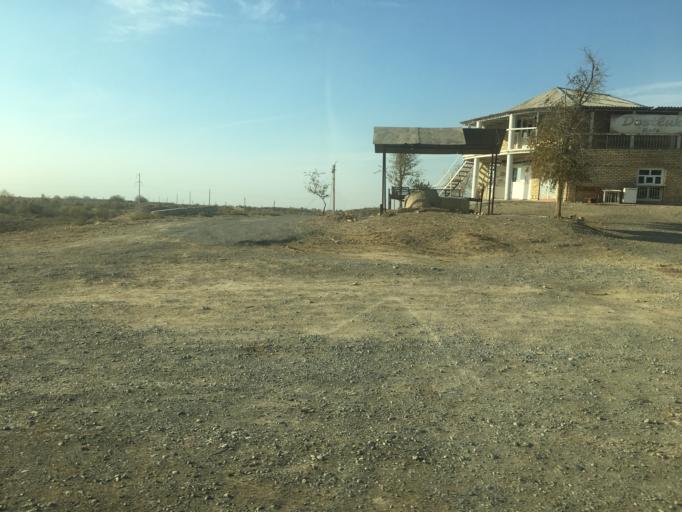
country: TM
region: Mary
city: Mary
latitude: 37.4690
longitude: 61.3296
